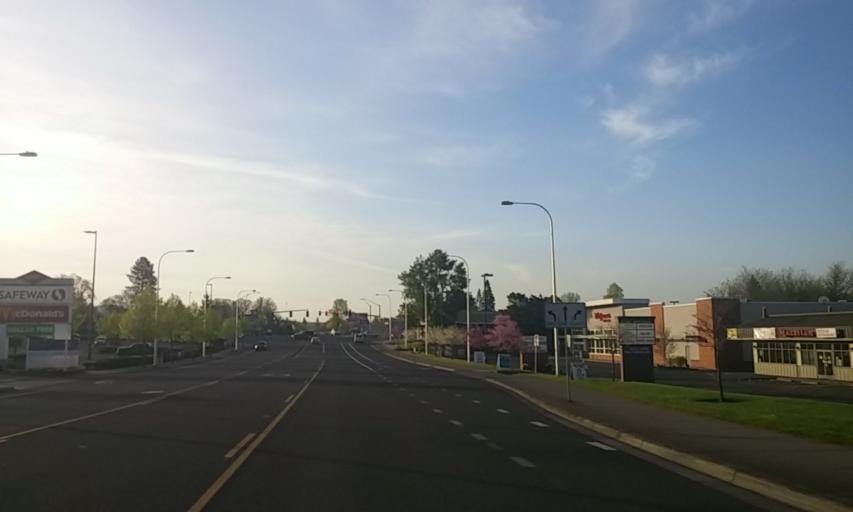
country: US
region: Oregon
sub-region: Washington County
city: Cedar Mill
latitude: 45.5274
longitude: -122.8160
